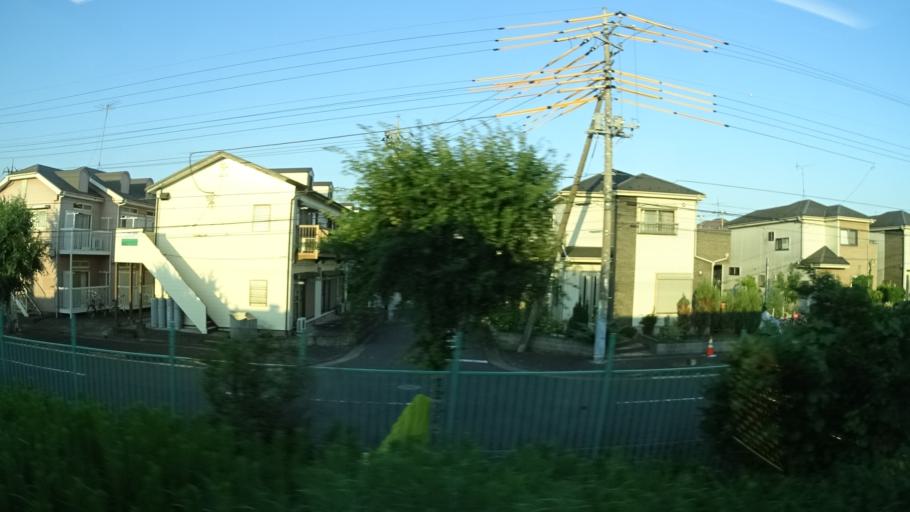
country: JP
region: Ibaraki
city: Ushiku
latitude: 35.9377
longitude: 140.1383
